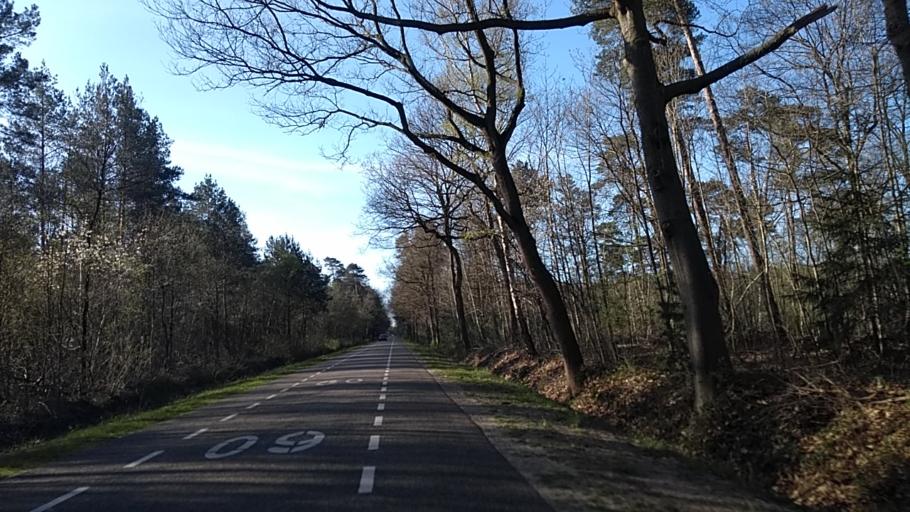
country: NL
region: Overijssel
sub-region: Gemeente Hof van Twente
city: Delden
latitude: 52.2733
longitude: 6.6697
